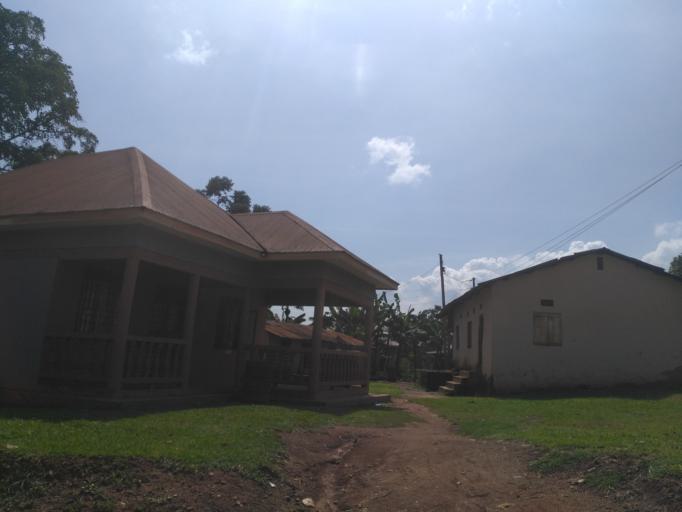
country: UG
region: Central Region
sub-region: Wakiso District
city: Kireka
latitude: 0.4470
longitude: 32.5808
